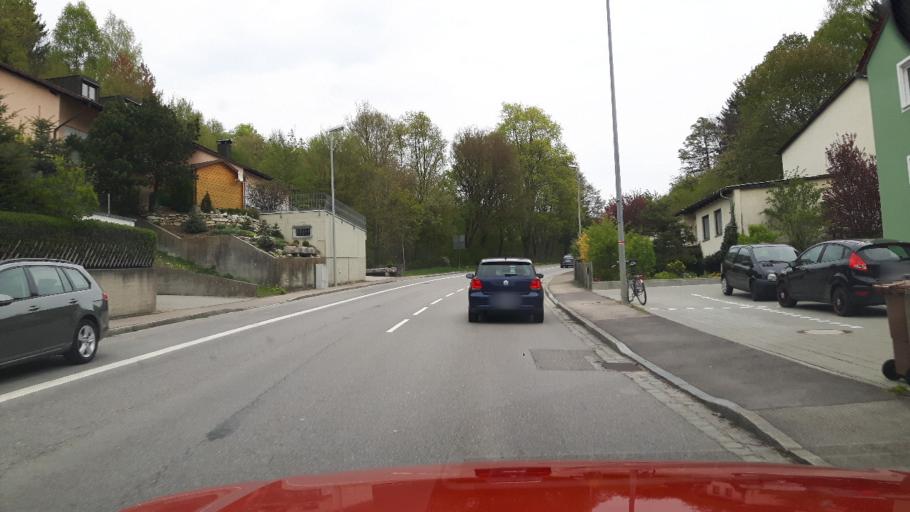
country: DE
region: Bavaria
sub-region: Upper Bavaria
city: Eichstaett
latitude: 48.8883
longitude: 11.2067
